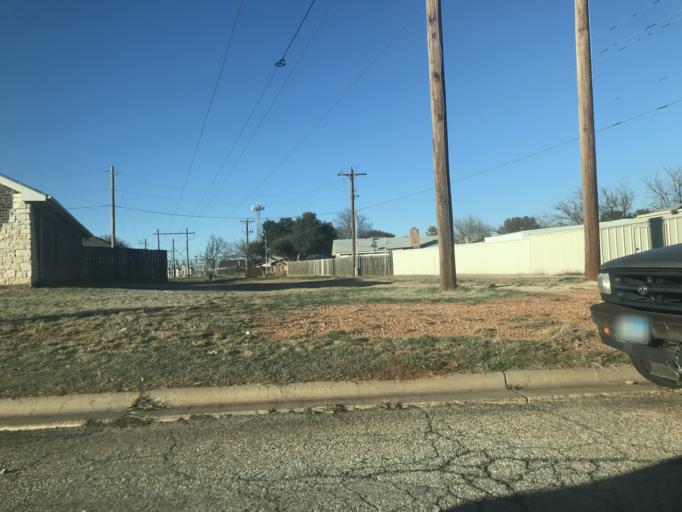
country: US
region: Texas
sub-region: Tom Green County
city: San Angelo
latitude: 31.4307
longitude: -100.4954
